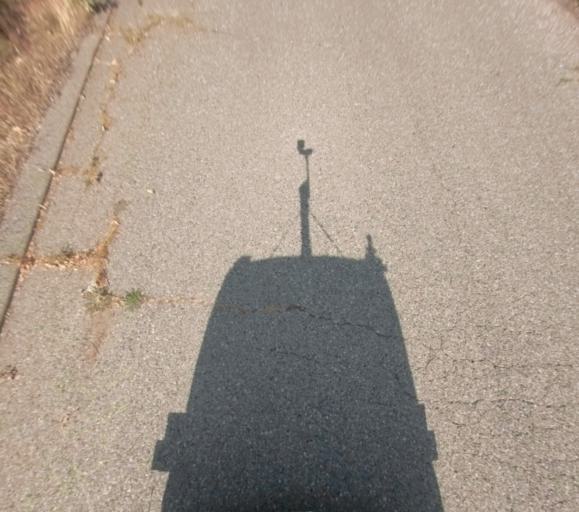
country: US
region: California
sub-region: Fresno County
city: Auberry
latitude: 37.2217
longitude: -119.5327
